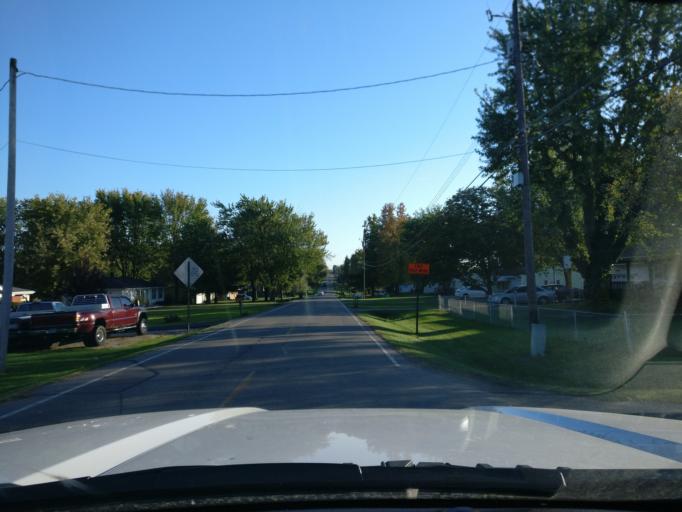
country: US
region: Ohio
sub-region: Warren County
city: Hunter
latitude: 39.5201
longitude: -84.2758
